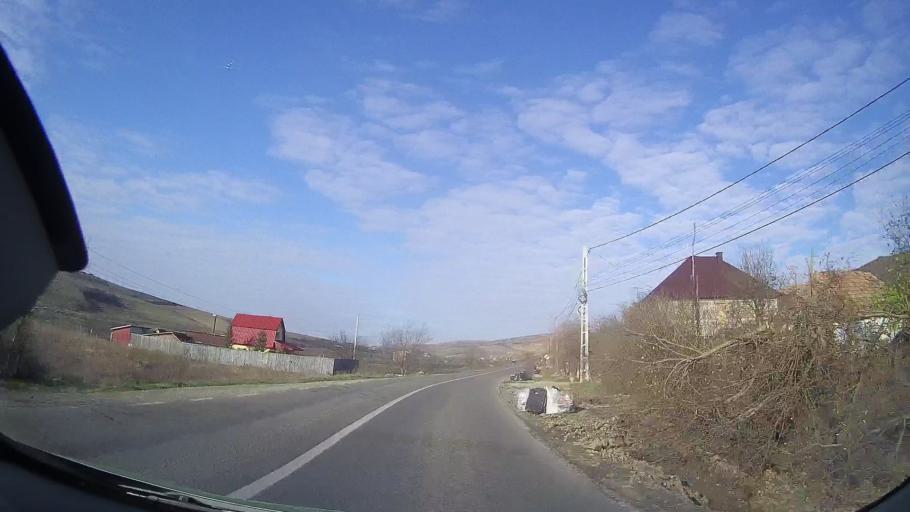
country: RO
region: Cluj
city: Caianu Mic
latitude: 46.8001
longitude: 23.8744
